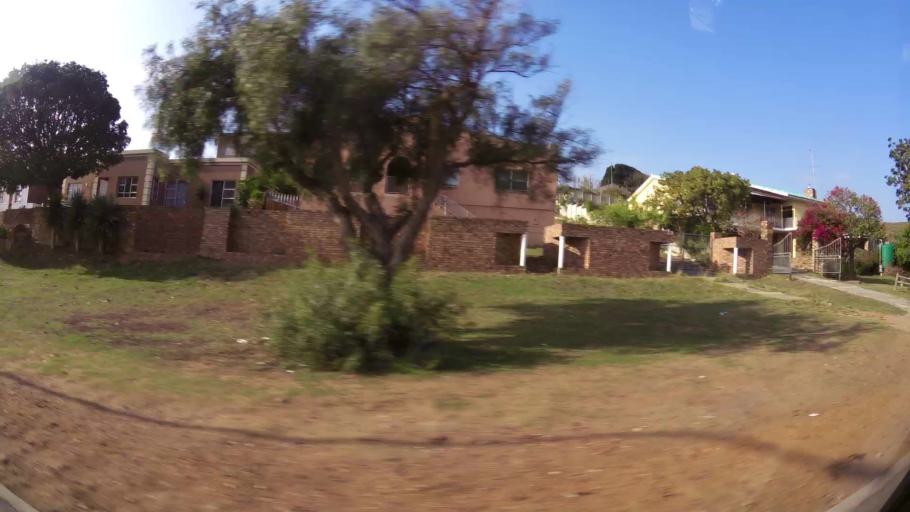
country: ZA
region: Eastern Cape
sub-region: Nelson Mandela Bay Metropolitan Municipality
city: Port Elizabeth
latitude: -33.9236
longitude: 25.5512
